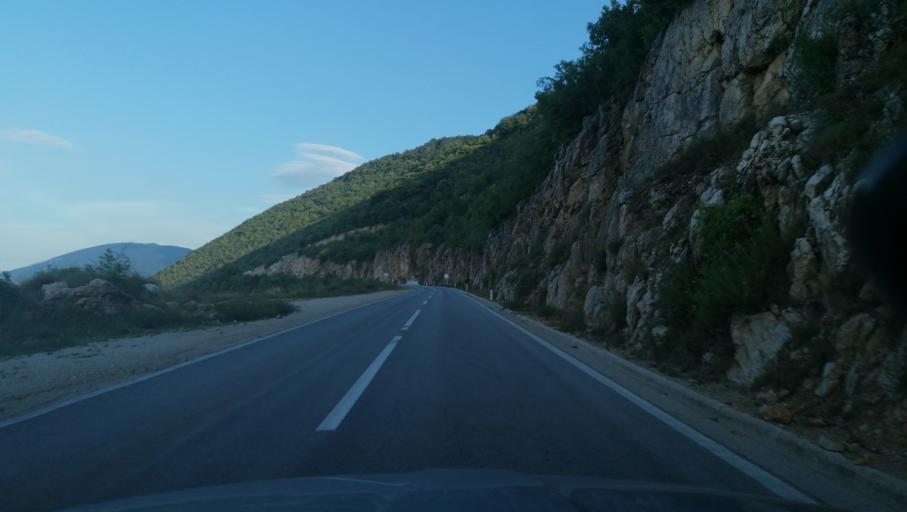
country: BA
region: Federation of Bosnia and Herzegovina
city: Prozor
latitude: 43.8374
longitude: 17.5874
